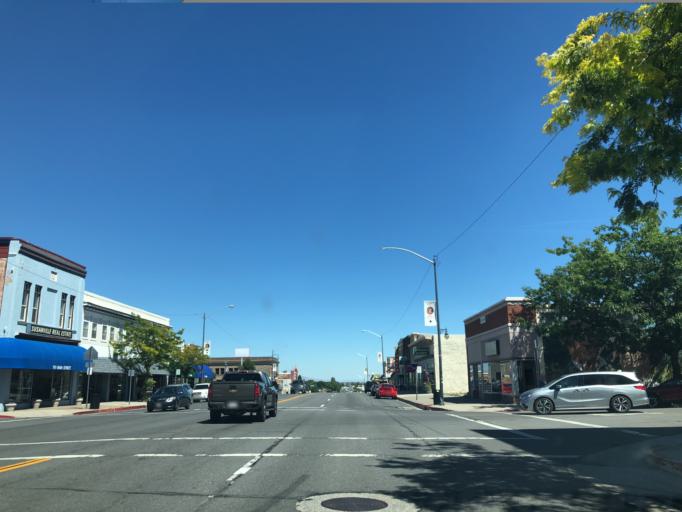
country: US
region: California
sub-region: Lassen County
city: Susanville
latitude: 40.4186
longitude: -120.6623
